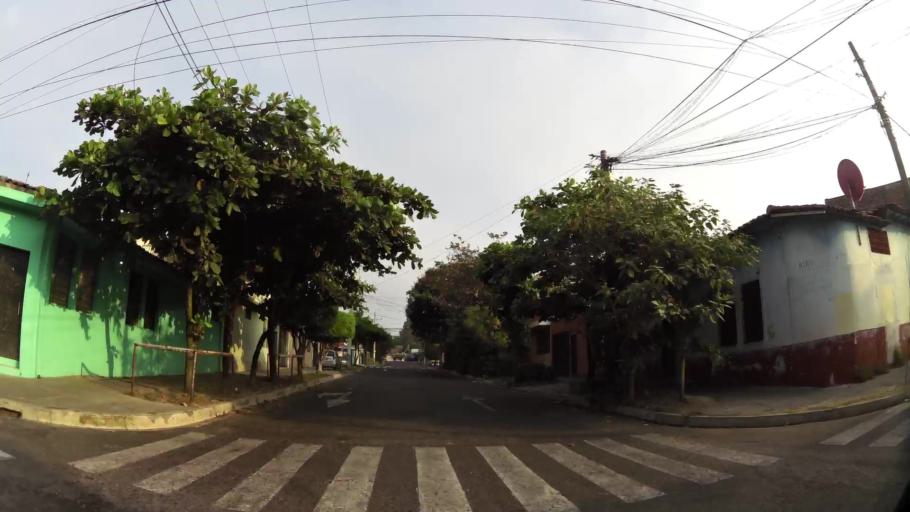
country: SV
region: San Salvador
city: San Salvador
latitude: 13.6911
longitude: -89.2027
